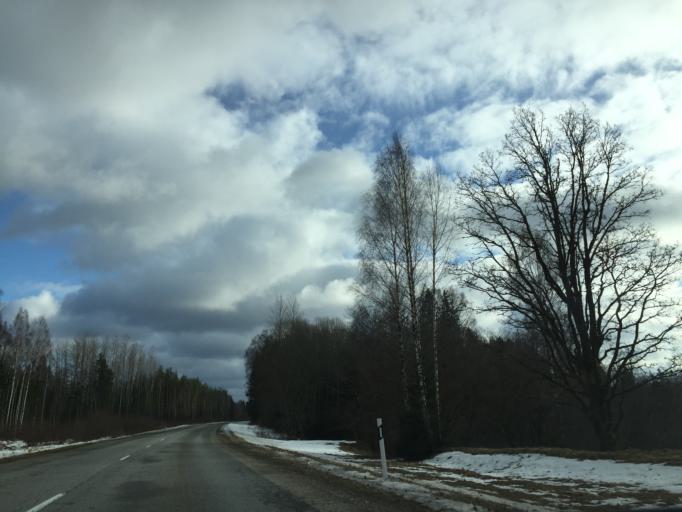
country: LV
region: Aloja
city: Staicele
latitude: 57.8612
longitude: 24.6985
